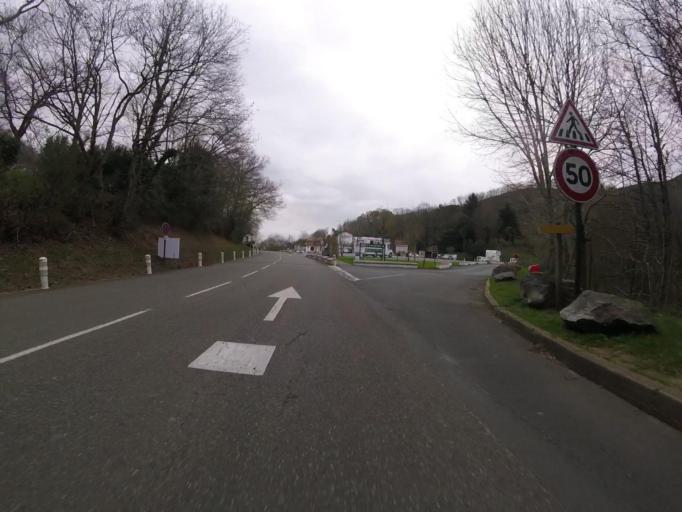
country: FR
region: Aquitaine
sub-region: Departement des Pyrenees-Atlantiques
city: Sare
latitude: 43.3261
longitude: -1.6011
